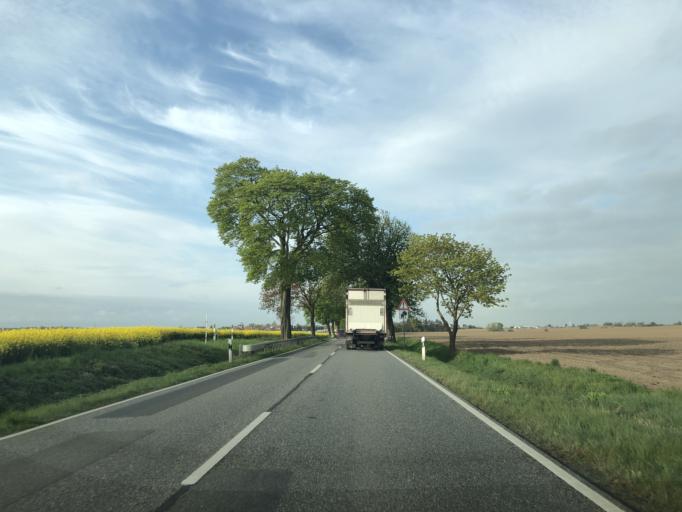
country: DE
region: Mecklenburg-Vorpommern
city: Guestrow
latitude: 53.8518
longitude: 12.2258
